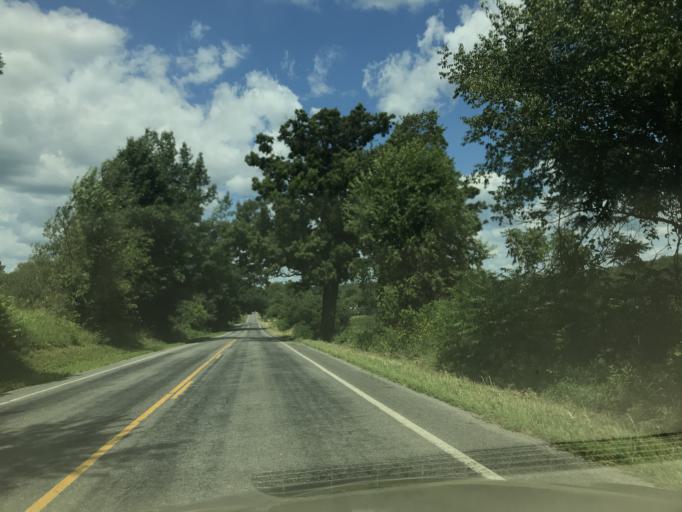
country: US
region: Michigan
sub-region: Eaton County
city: Eaton Rapids
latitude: 42.4584
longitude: -84.5606
